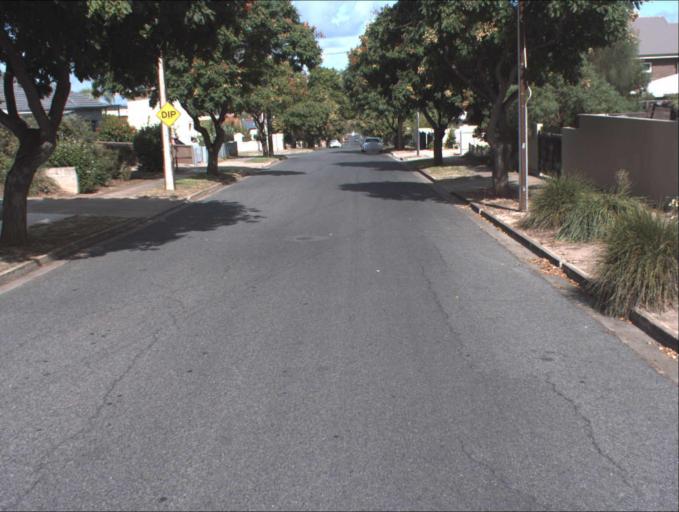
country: AU
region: South Australia
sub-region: Port Adelaide Enfield
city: Blair Athol
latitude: -34.8629
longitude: 138.5979
